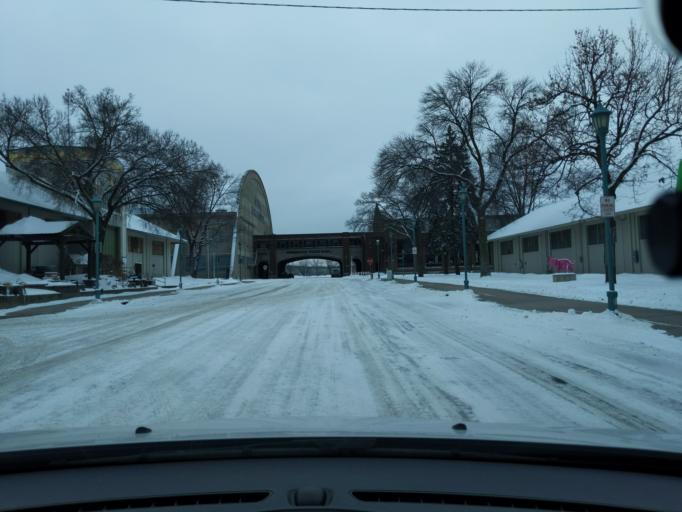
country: US
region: Minnesota
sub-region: Ramsey County
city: Falcon Heights
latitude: 44.9794
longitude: -93.1754
